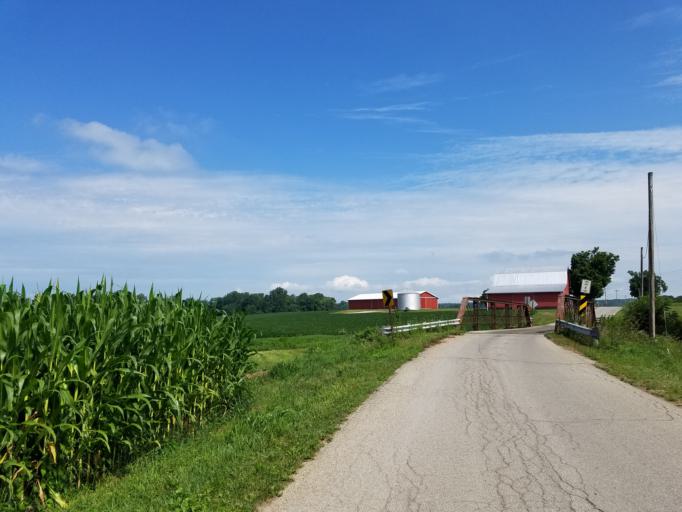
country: US
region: Ohio
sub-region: Knox County
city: Fredericktown
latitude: 40.4589
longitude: -82.6565
